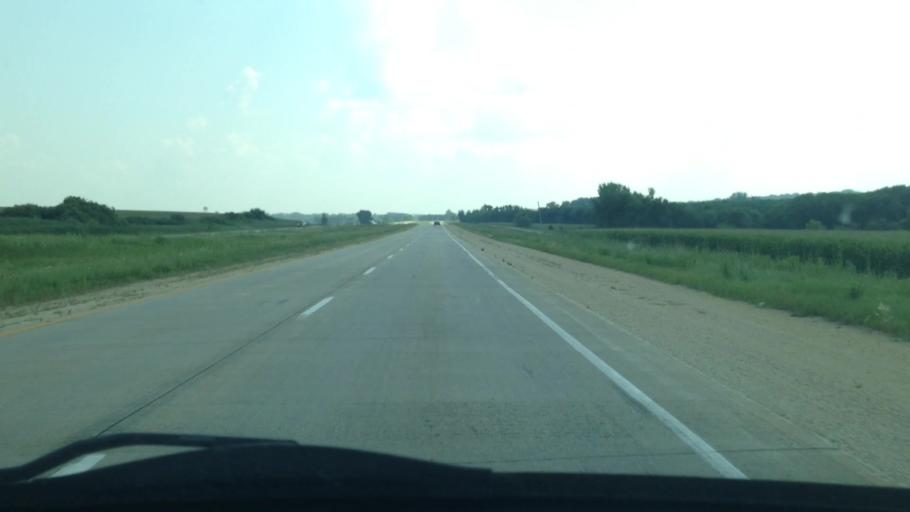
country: US
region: Iowa
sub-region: Bremer County
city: Denver
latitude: 42.6974
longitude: -92.3380
